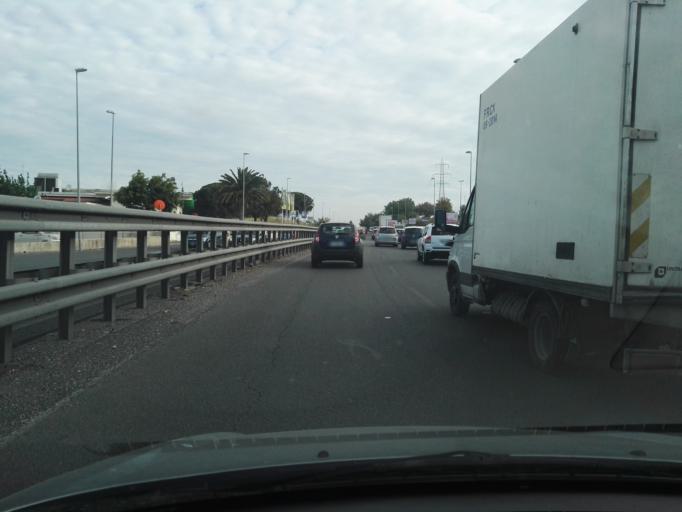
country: IT
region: Latium
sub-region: Citta metropolitana di Roma Capitale
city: Selcetta
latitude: 41.7920
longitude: 12.4808
